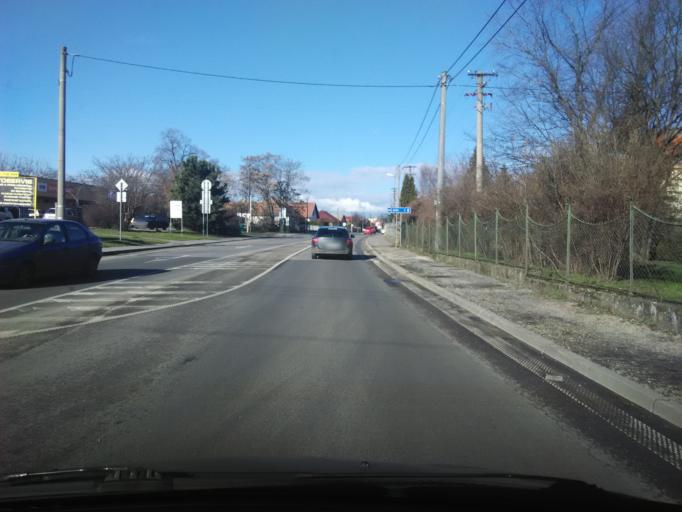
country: SK
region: Nitriansky
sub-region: Okres Nitra
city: Nitra
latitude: 48.2384
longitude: 18.1196
